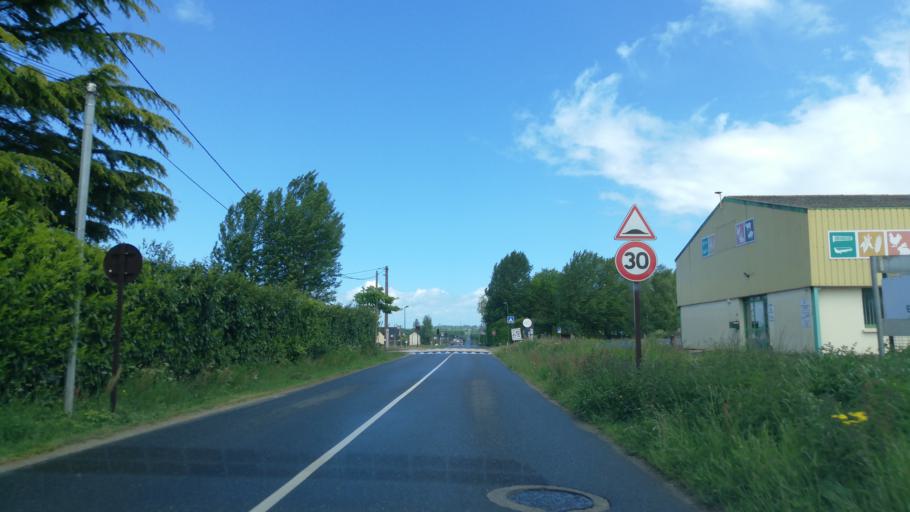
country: FR
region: Brittany
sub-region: Departement d'Ille-et-Vilaine
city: Irodouer
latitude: 48.2433
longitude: -1.9487
